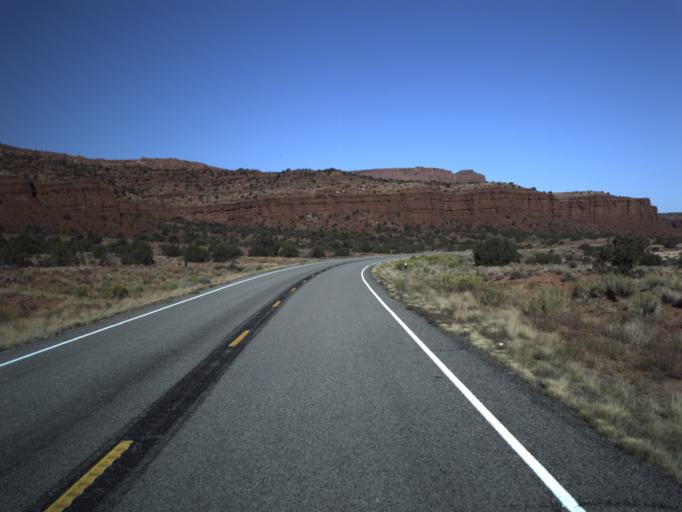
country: US
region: Utah
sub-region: San Juan County
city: Blanding
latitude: 37.6786
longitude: -110.2154
